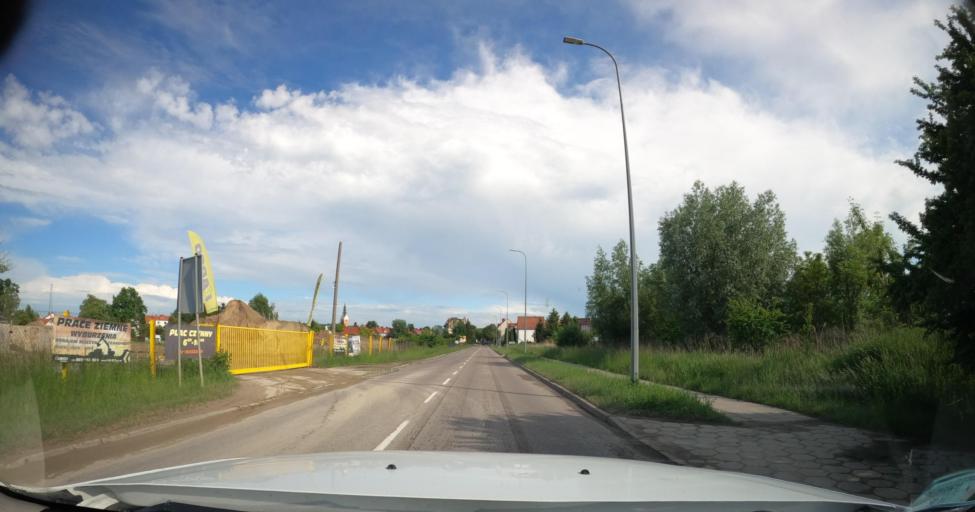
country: PL
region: Warmian-Masurian Voivodeship
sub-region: Powiat elblaski
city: Elblag
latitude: 54.1625
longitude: 19.3816
